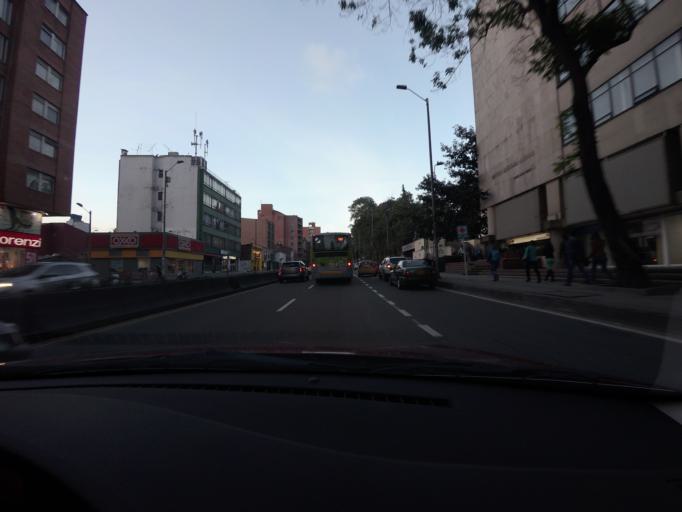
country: CO
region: Bogota D.C.
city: Bogota
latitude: 4.6285
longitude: -74.0651
